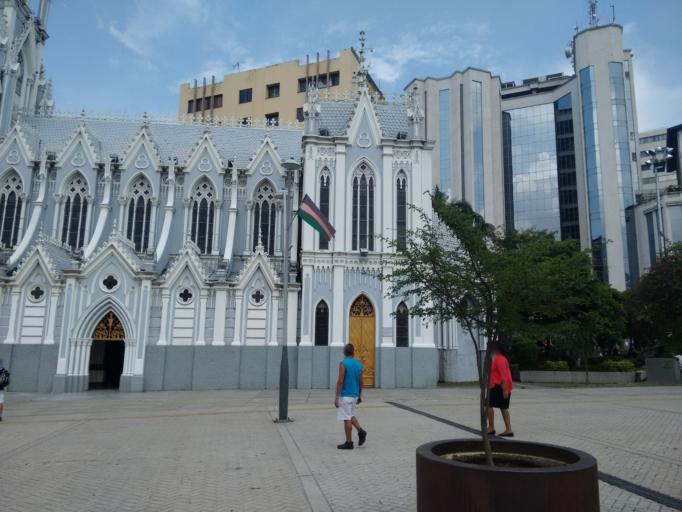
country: CO
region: Valle del Cauca
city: Cali
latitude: 3.4541
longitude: -76.5322
